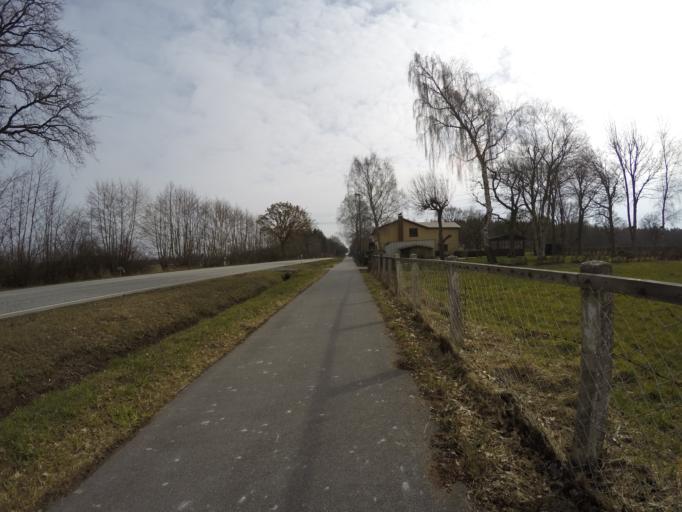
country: DE
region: Schleswig-Holstein
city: Bilsen
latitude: 53.7606
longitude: 9.8799
